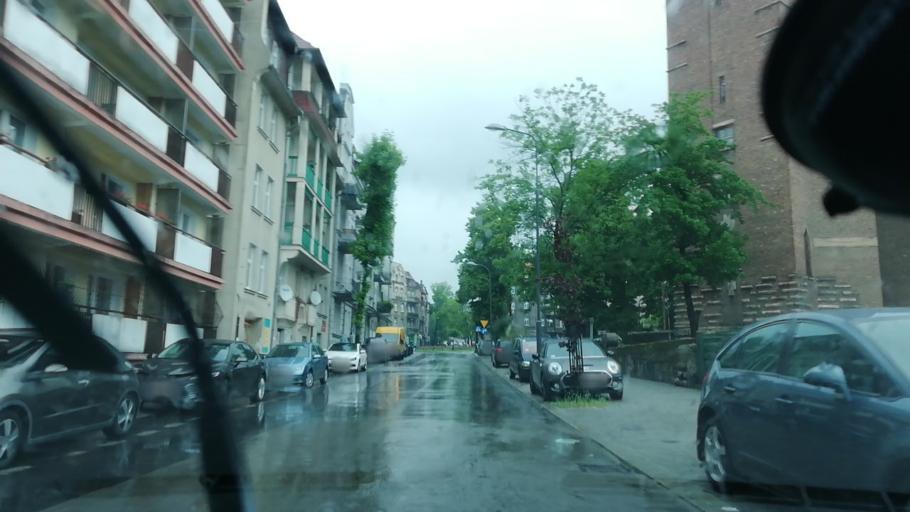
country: PL
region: Silesian Voivodeship
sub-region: Chorzow
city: Chorzow
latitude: 50.2933
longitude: 18.9527
